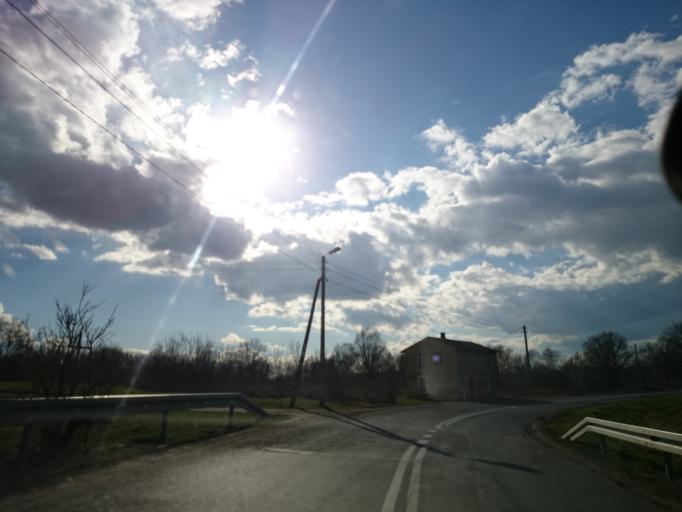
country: PL
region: Opole Voivodeship
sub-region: Powiat nyski
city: Sidzina
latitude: 50.6431
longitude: 17.4873
